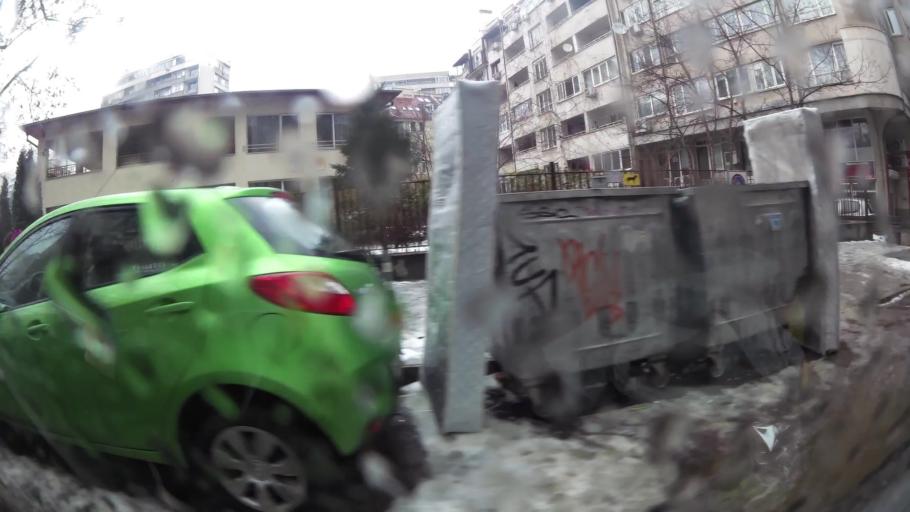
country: BG
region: Sofia-Capital
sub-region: Stolichna Obshtina
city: Sofia
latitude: 42.6755
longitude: 23.2988
